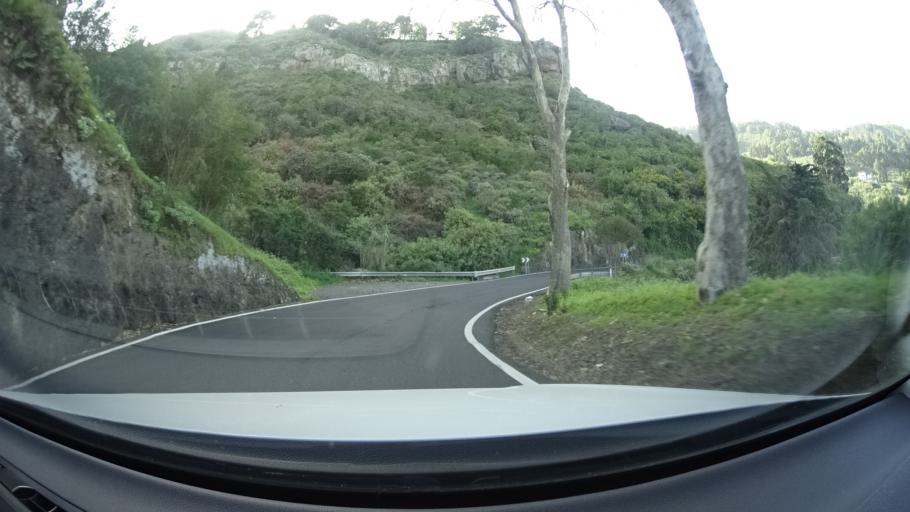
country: ES
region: Canary Islands
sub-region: Provincia de Las Palmas
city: Teror
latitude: 28.0553
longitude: -15.5556
